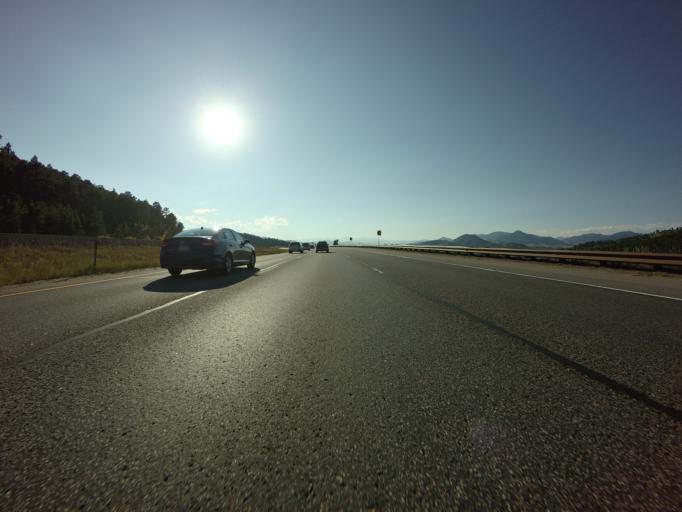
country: US
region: Colorado
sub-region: Jefferson County
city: Genesee
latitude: 39.7141
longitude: -105.3095
